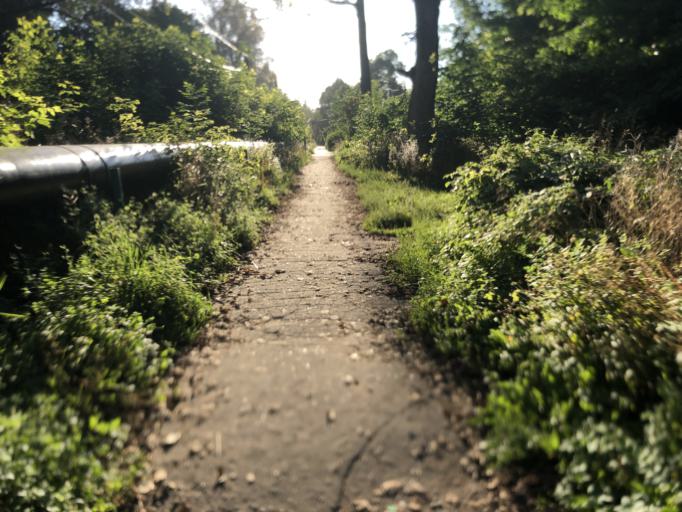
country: RU
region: Tverskaya
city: Rzhev
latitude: 56.2437
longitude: 34.3286
